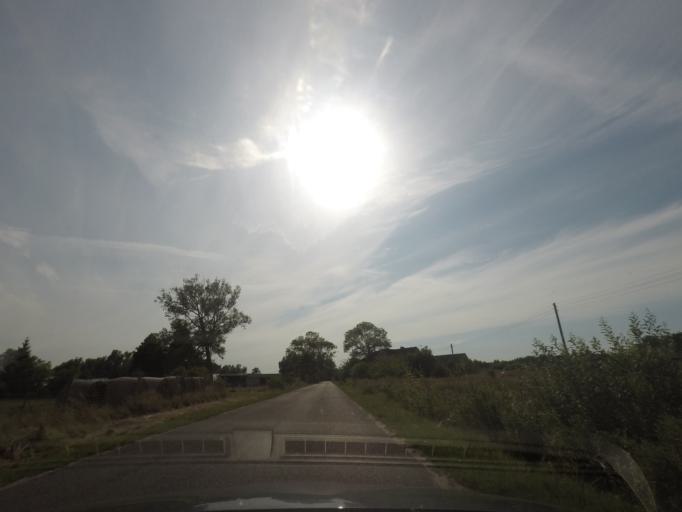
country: PL
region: Pomeranian Voivodeship
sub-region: Powiat slupski
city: Smoldzino
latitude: 54.6313
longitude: 17.2541
